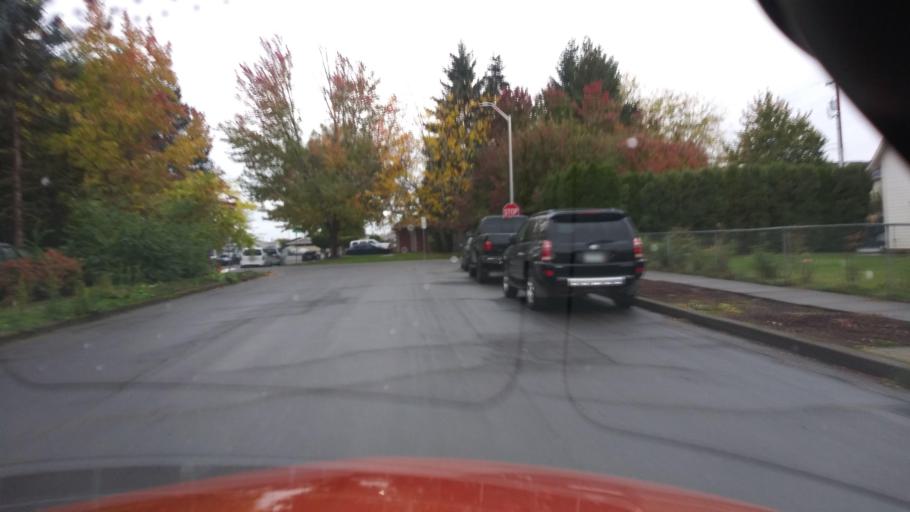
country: US
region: Oregon
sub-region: Washington County
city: Cornelius
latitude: 45.5238
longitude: -123.0353
